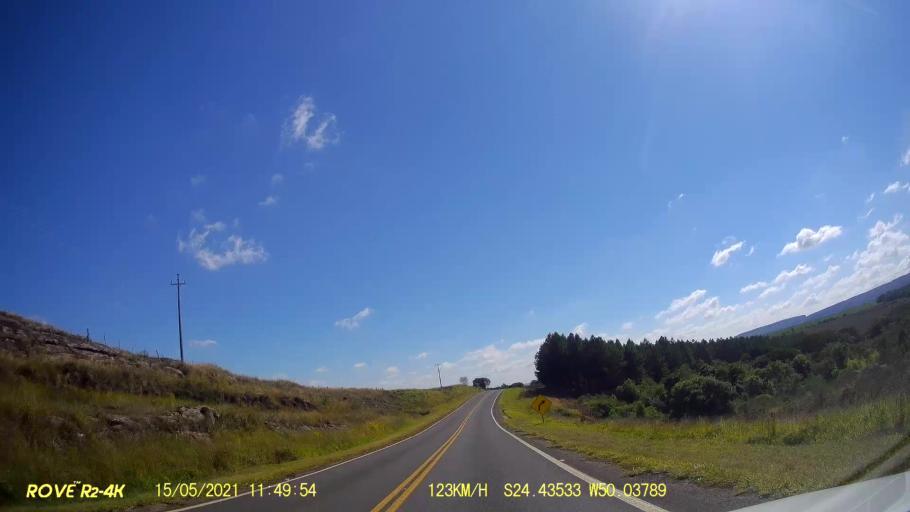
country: BR
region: Parana
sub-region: Pirai Do Sul
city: Pirai do Sul
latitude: -24.4357
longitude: -50.0377
